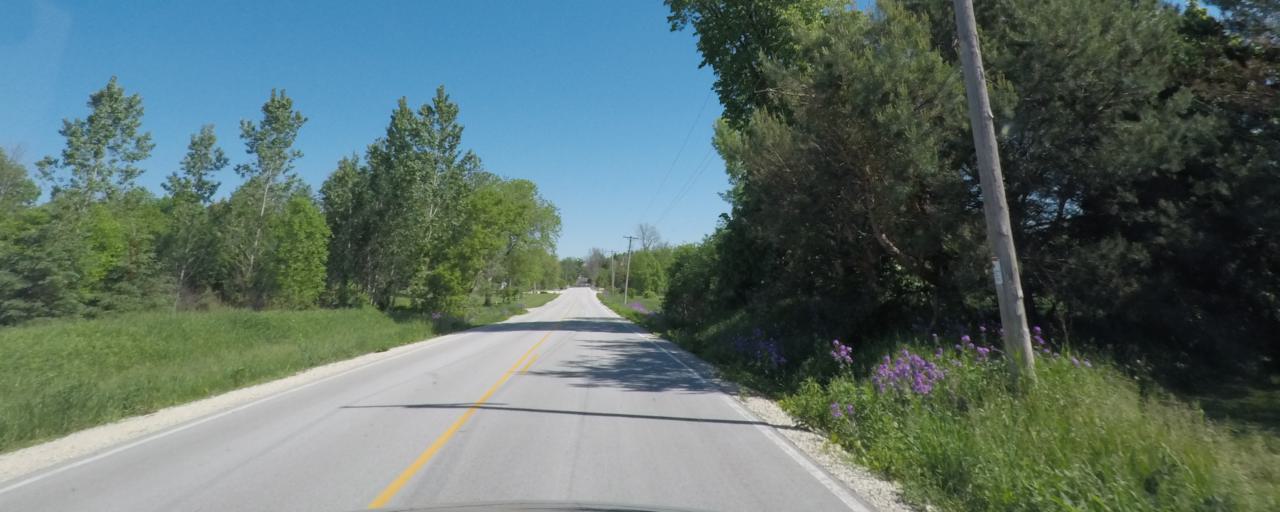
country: US
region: Wisconsin
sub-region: Sheboygan County
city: Sheboygan Falls
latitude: 43.7393
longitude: -87.8402
